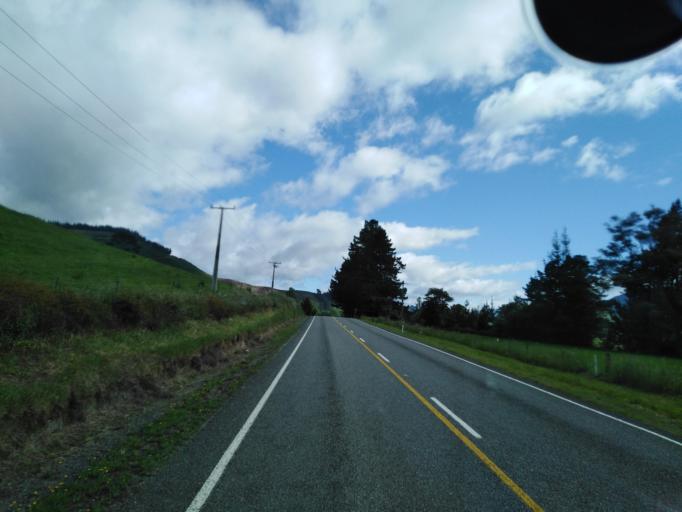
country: NZ
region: Nelson
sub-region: Nelson City
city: Nelson
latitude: -41.2744
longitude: 173.5730
